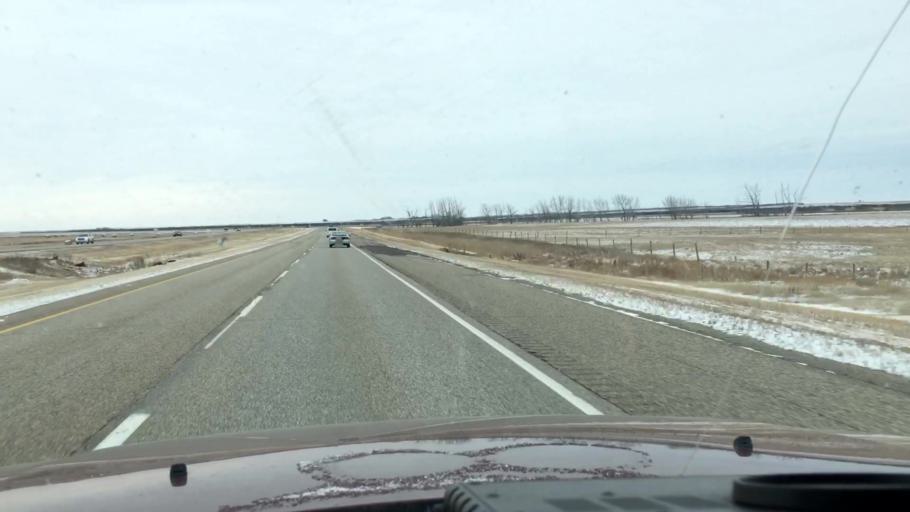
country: CA
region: Saskatchewan
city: Saskatoon
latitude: 51.4809
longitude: -106.2503
